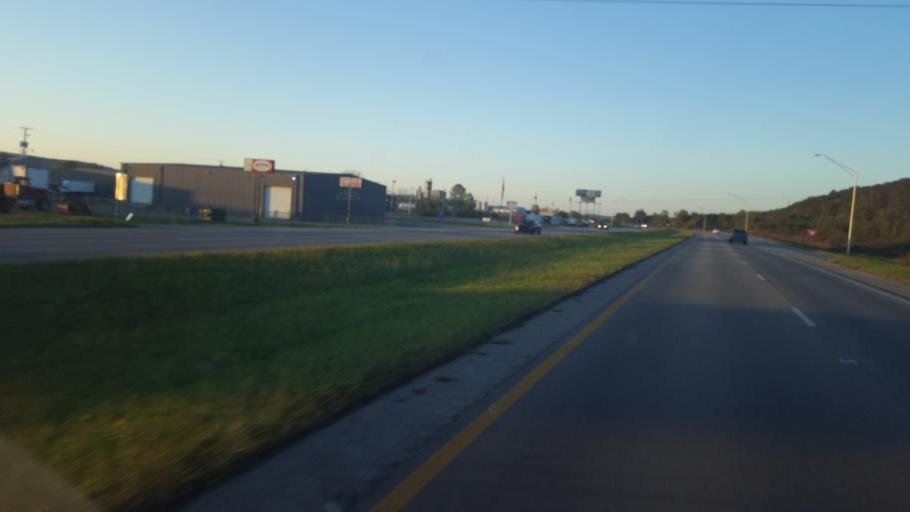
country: US
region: Ohio
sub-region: Pike County
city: Piketon
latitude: 39.0150
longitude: -83.0257
